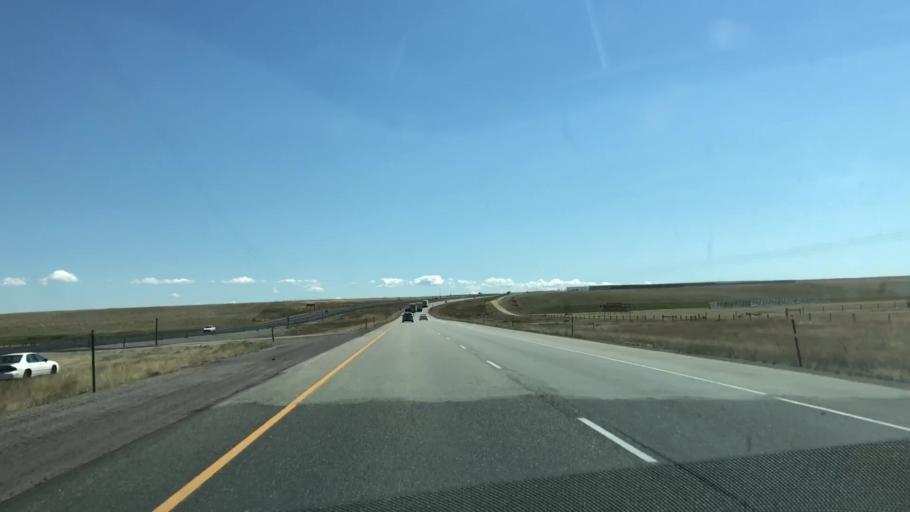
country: US
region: Wyoming
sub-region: Albany County
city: Laramie
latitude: 41.5548
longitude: -106.0983
